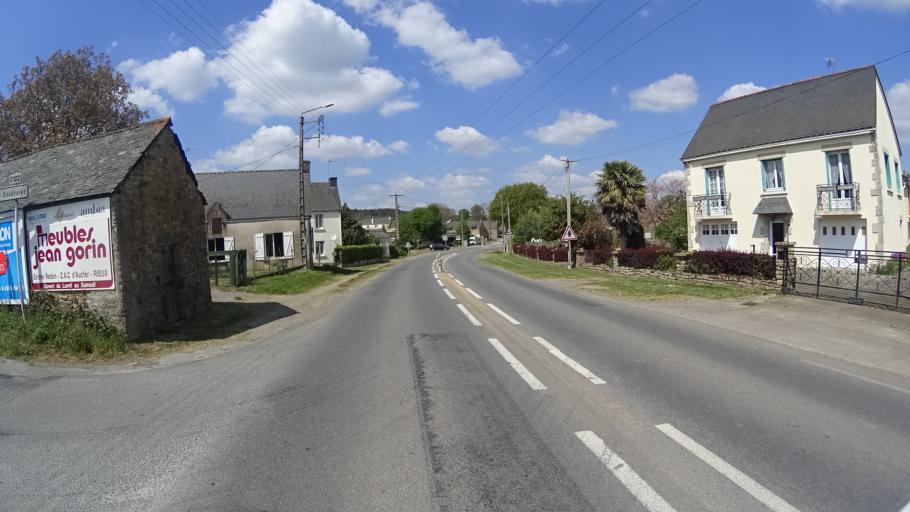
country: FR
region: Brittany
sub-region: Departement du Morbihan
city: Rieux
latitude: 47.6103
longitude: -2.1120
